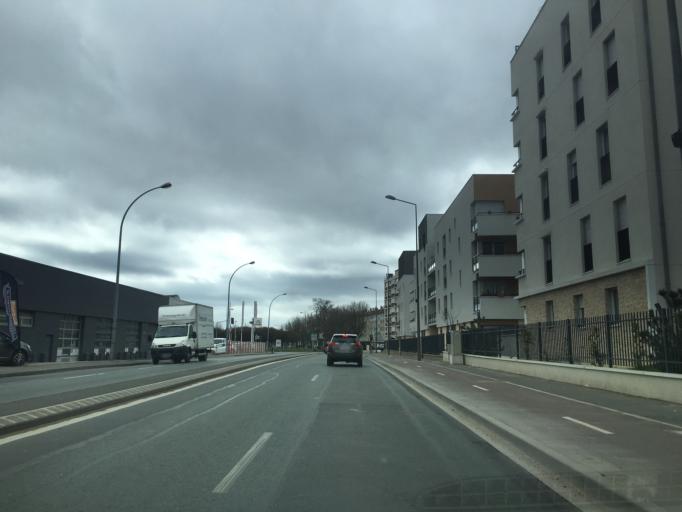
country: FR
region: Ile-de-France
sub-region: Departement du Val-de-Marne
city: Bonneuil-sur-Marne
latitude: 48.7748
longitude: 2.4899
